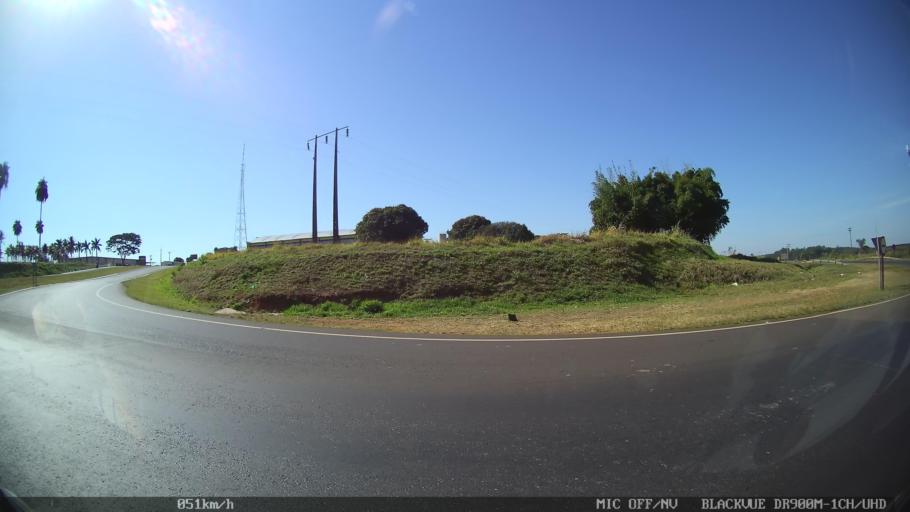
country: BR
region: Sao Paulo
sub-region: Batatais
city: Batatais
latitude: -20.9014
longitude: -47.6047
